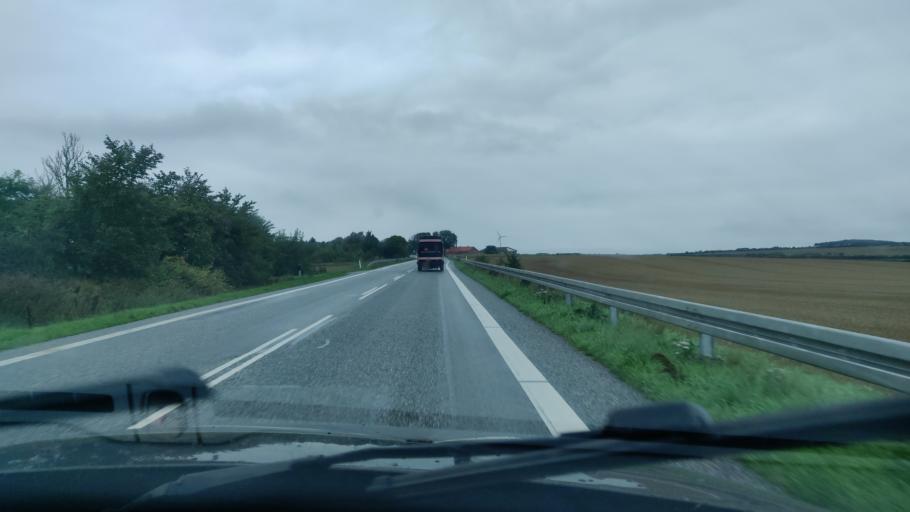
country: DK
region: North Denmark
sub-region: Thisted Kommune
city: Thisted
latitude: 56.9836
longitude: 8.7655
